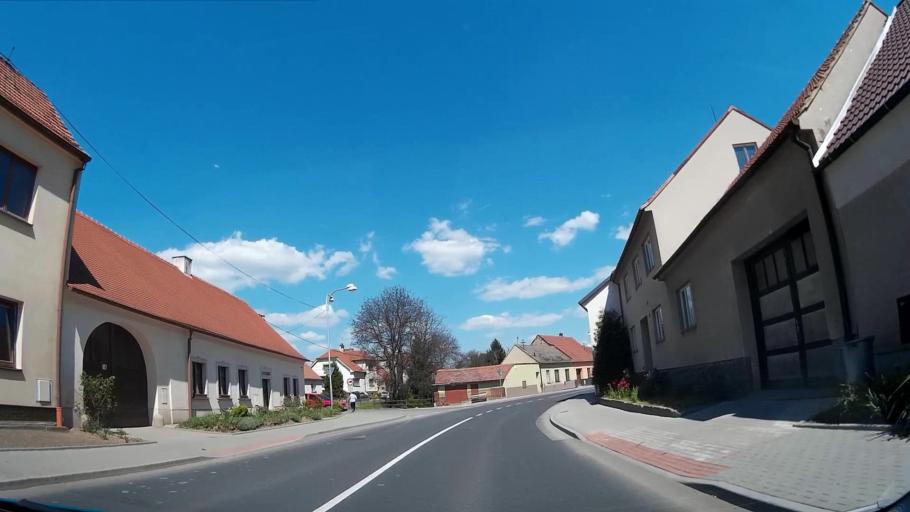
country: CZ
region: South Moravian
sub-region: Okres Brno-Venkov
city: Rosice
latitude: 49.1434
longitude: 16.3873
